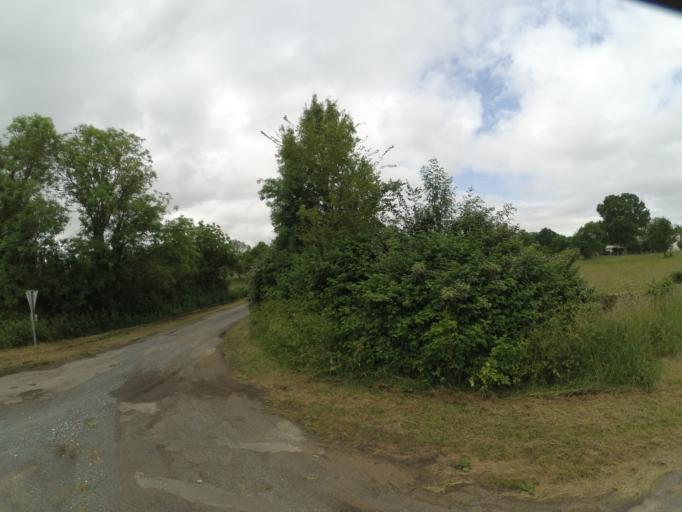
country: FR
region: Poitou-Charentes
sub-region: Departement de la Charente-Maritime
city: Saint-Laurent-de-la-Pree
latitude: 45.9946
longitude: -1.0350
